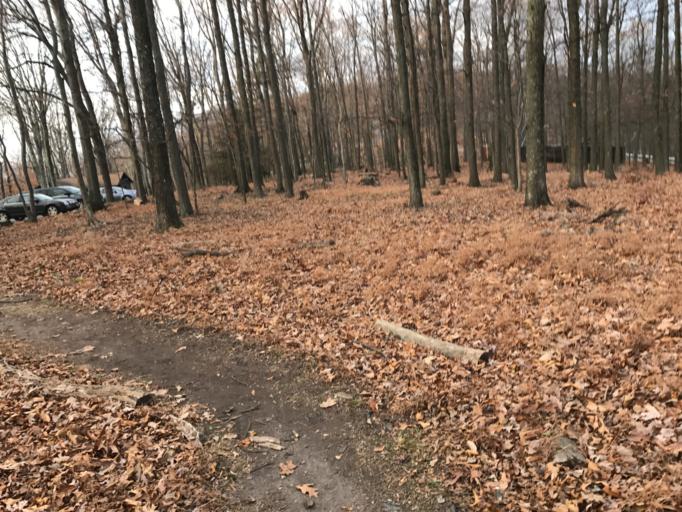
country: US
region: Maryland
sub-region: Frederick County
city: Braddock Heights
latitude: 39.4641
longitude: -77.4949
